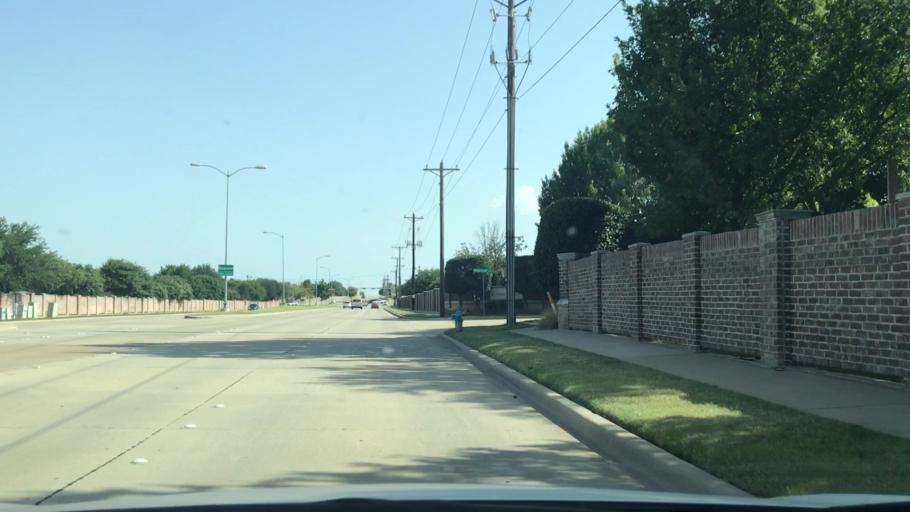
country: US
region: Texas
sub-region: Collin County
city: Frisco
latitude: 33.1150
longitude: -96.7510
